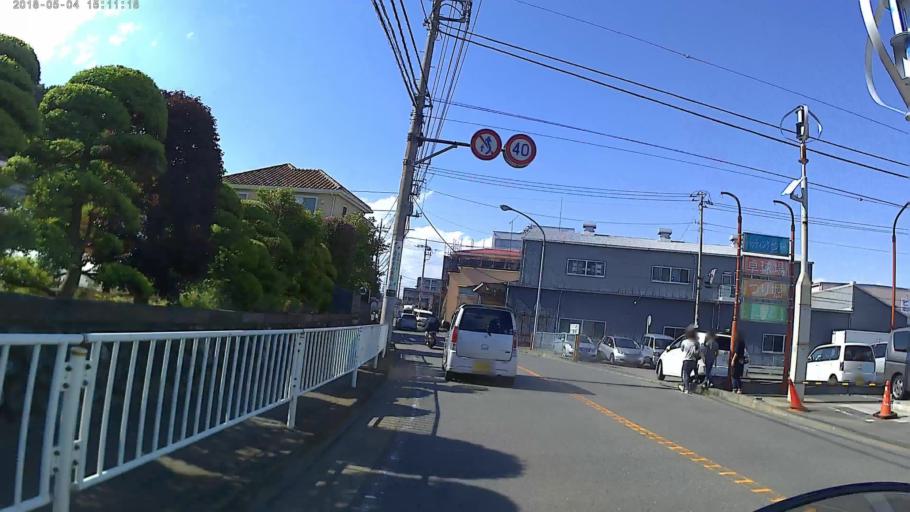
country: JP
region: Kanagawa
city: Yokohama
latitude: 35.5247
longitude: 139.6104
